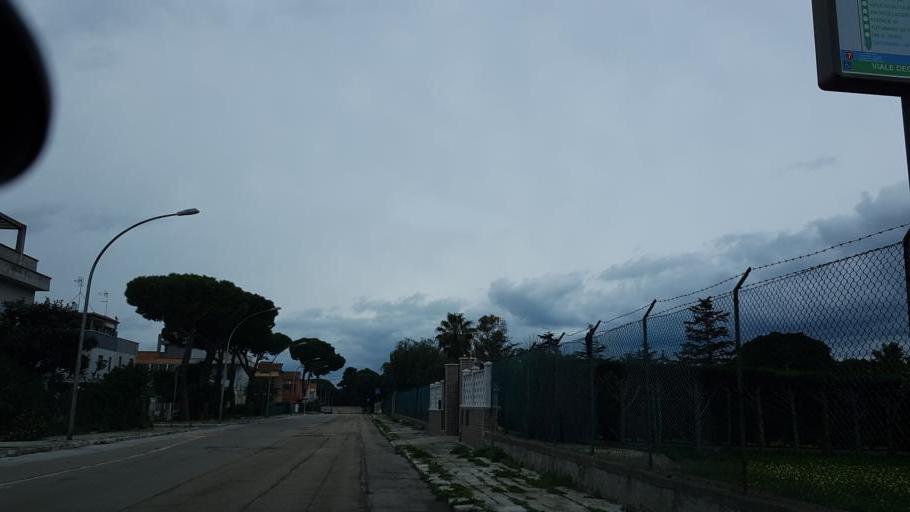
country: IT
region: Apulia
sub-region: Provincia di Brindisi
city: La Rosa
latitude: 40.6074
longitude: 17.9535
